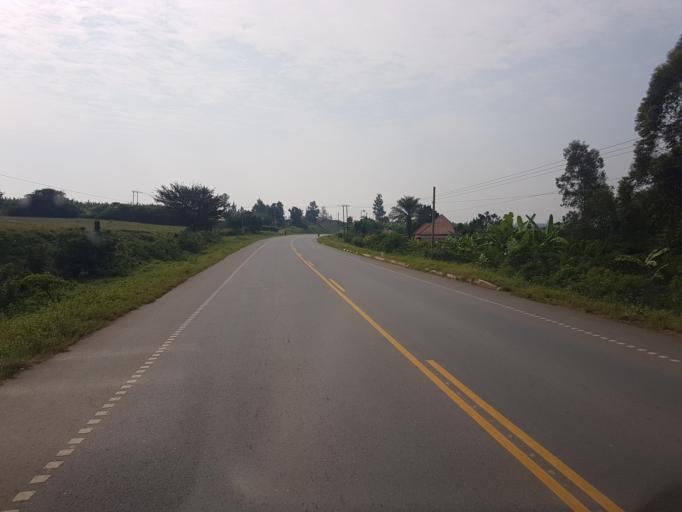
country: UG
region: Western Region
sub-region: Sheema District
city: Kibingo
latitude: -0.6348
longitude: 30.5353
